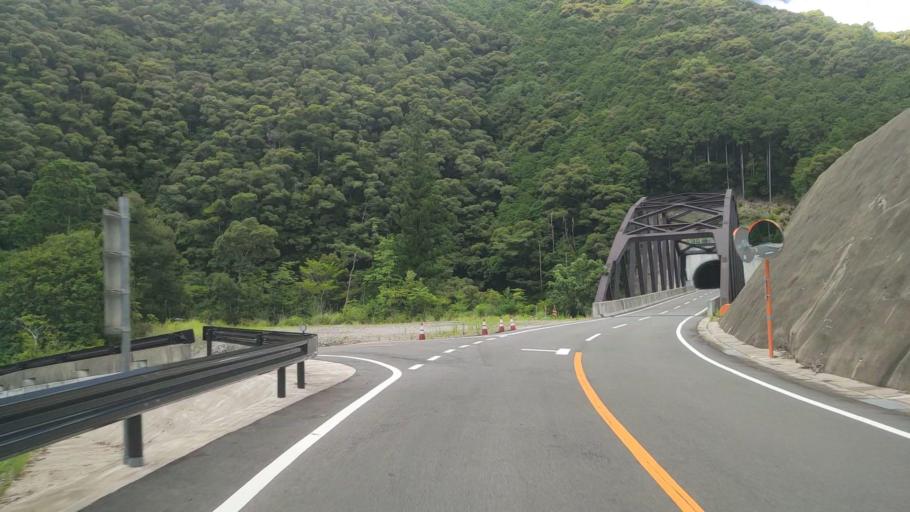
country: JP
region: Mie
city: Owase
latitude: 34.0022
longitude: 136.0092
